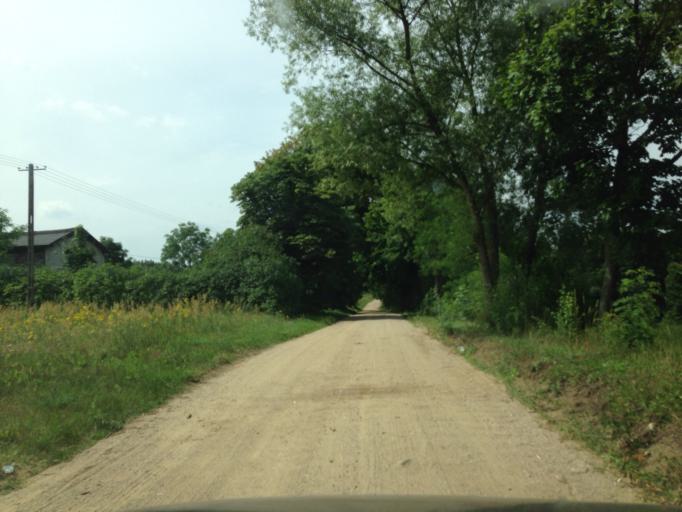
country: PL
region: Kujawsko-Pomorskie
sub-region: Powiat brodnicki
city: Bartniczka
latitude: 53.2751
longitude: 19.5030
